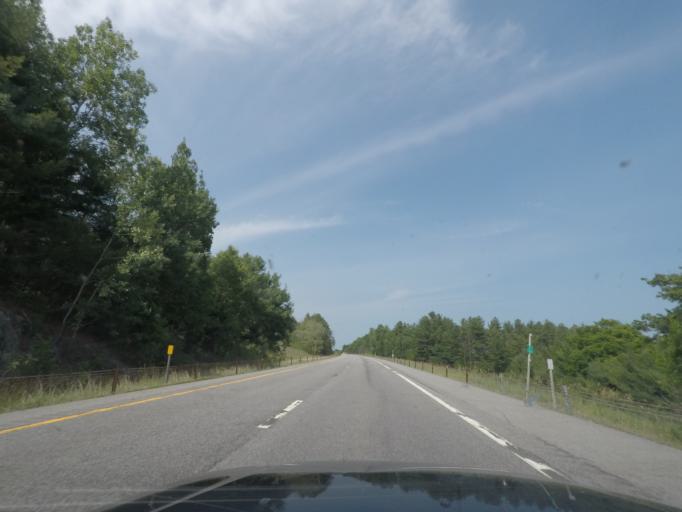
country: US
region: New York
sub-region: Essex County
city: Mineville
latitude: 44.1245
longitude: -73.5930
